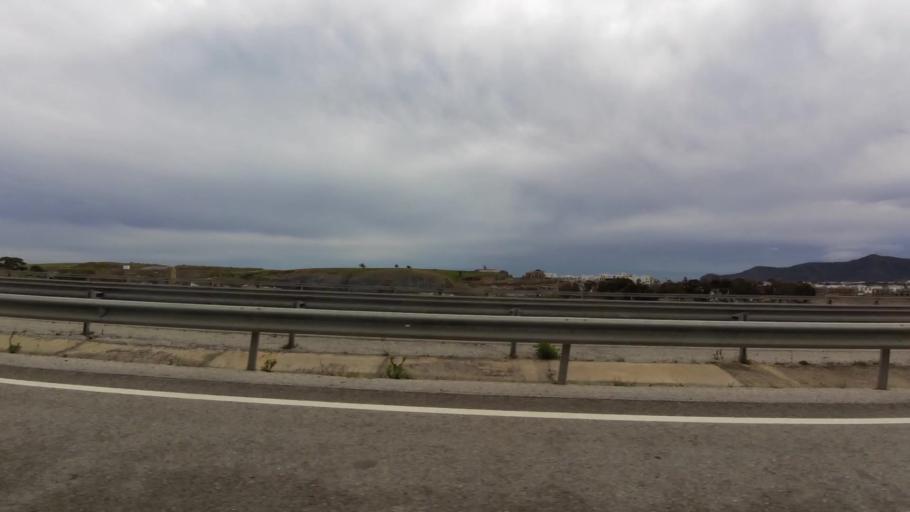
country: MA
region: Tanger-Tetouan
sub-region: Tetouan
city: Martil
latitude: 35.7219
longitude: -5.3532
